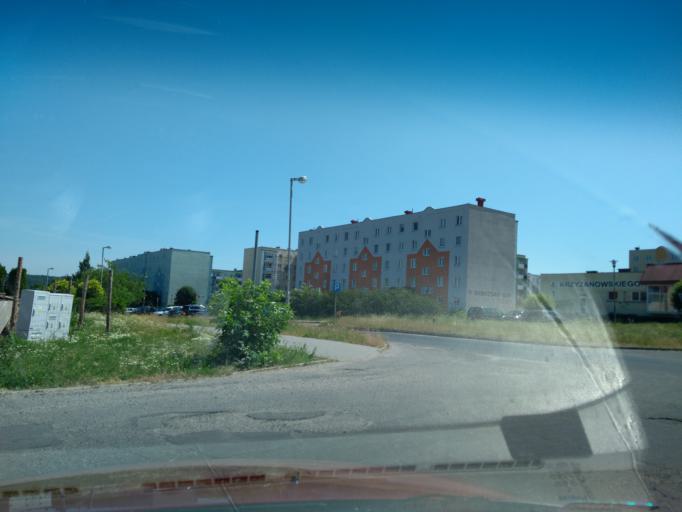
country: PL
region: West Pomeranian Voivodeship
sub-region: Koszalin
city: Koszalin
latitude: 54.2110
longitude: 16.1846
